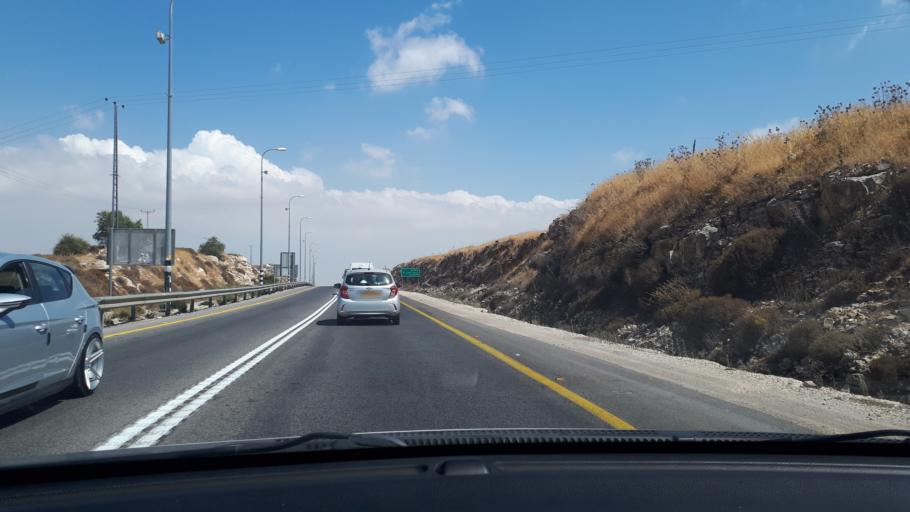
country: PS
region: West Bank
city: Burqah
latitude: 31.9095
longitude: 35.2519
